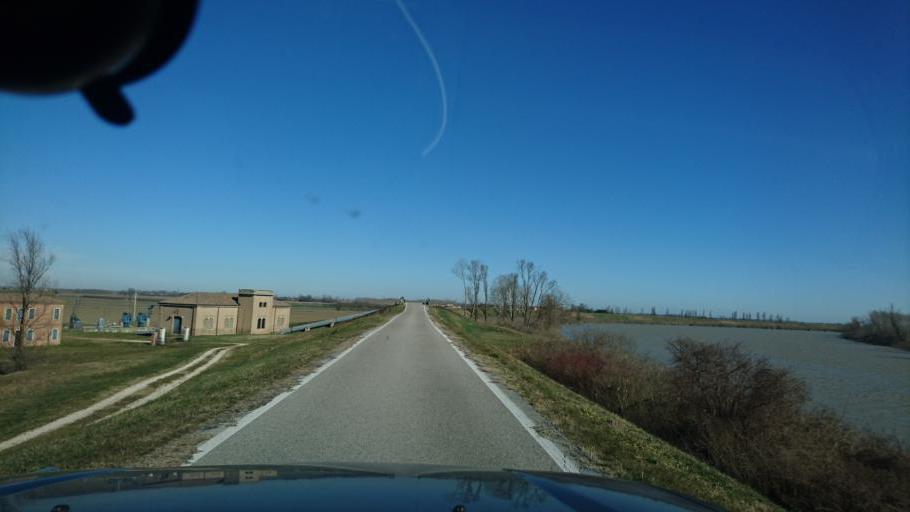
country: IT
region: Veneto
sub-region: Provincia di Rovigo
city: Ariano
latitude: 44.9414
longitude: 12.1649
